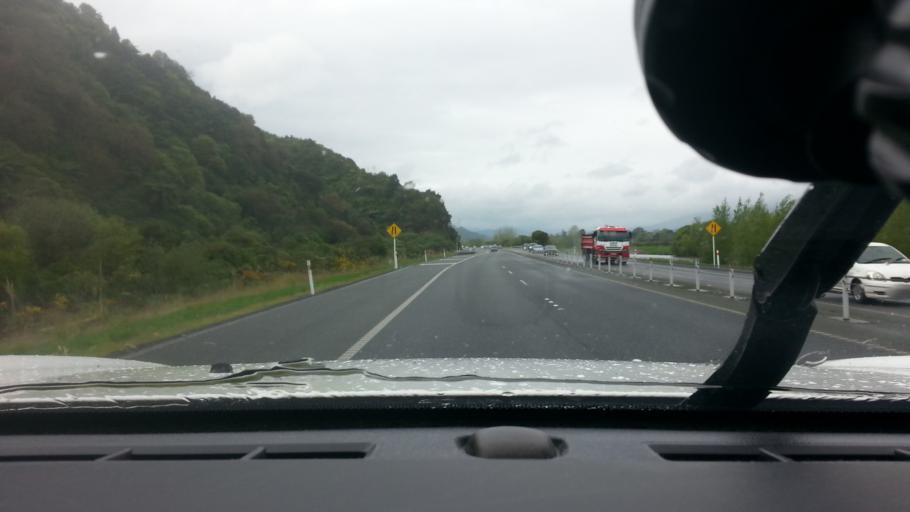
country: NZ
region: Wellington
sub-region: Upper Hutt City
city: Upper Hutt
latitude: -41.1402
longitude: 175.0036
